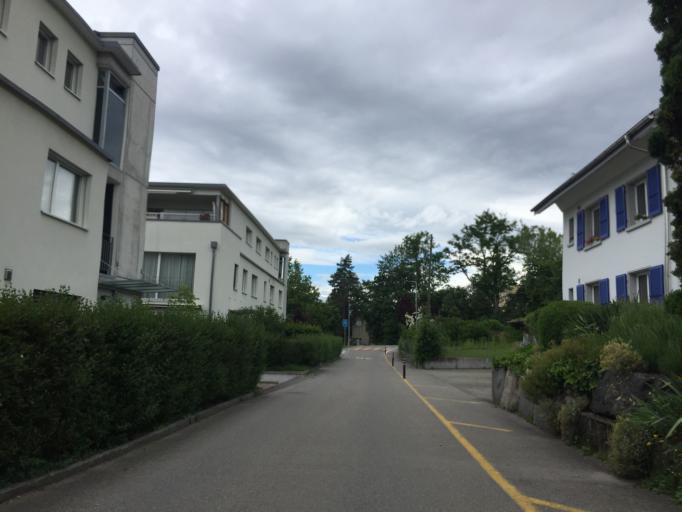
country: CH
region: Bern
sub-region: Bern-Mittelland District
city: Rubigen
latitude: 46.8993
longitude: 7.5467
